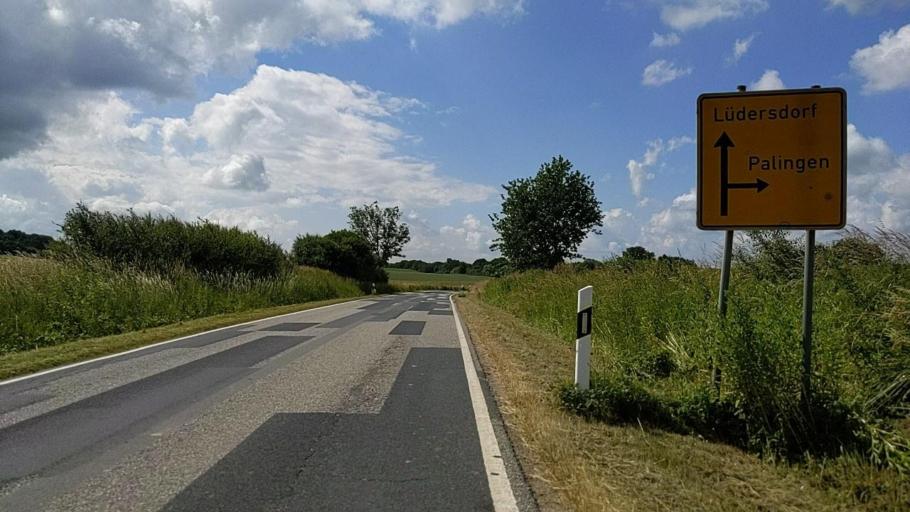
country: DE
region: Mecklenburg-Vorpommern
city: Selmsdorf
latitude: 53.8516
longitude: 10.8094
